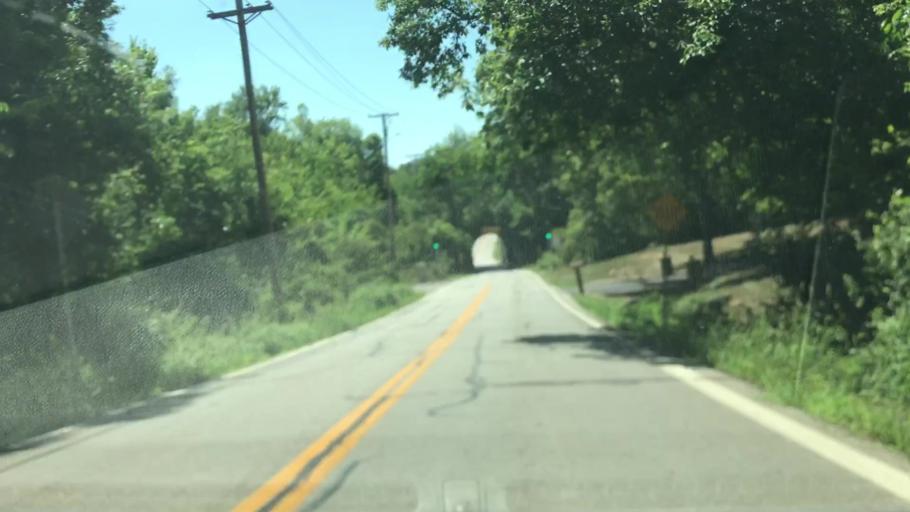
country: US
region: Missouri
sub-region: Jackson County
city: Lees Summit
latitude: 38.9274
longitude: -94.4361
